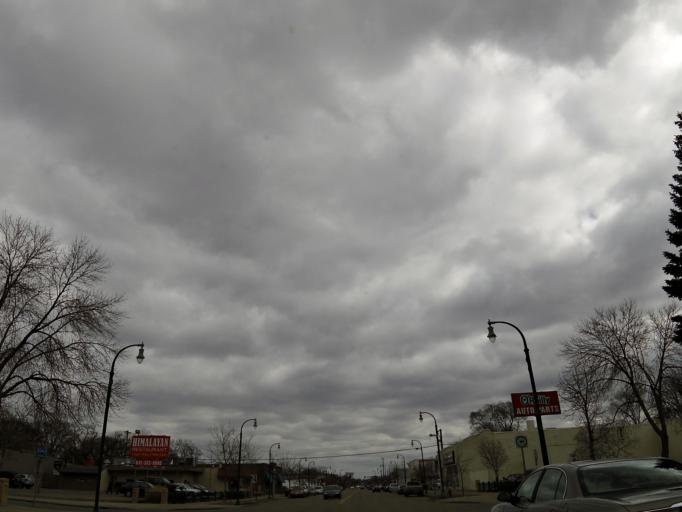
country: US
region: Minnesota
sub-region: Hennepin County
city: Minneapolis
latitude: 44.9484
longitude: -93.2305
